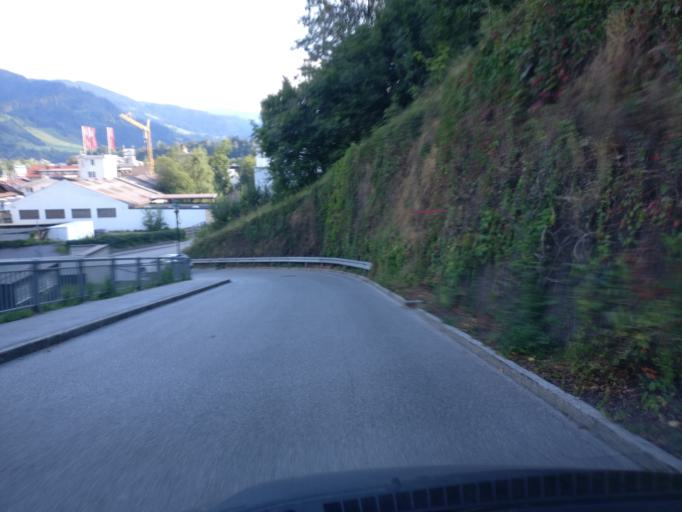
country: AT
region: Salzburg
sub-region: Politischer Bezirk Sankt Johann im Pongau
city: Bischofshofen
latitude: 47.4125
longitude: 13.2153
